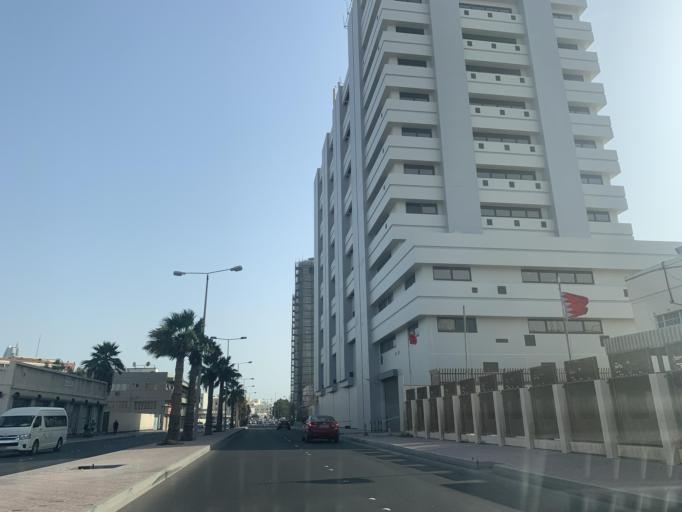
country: BH
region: Manama
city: Manama
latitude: 26.2218
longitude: 50.5695
